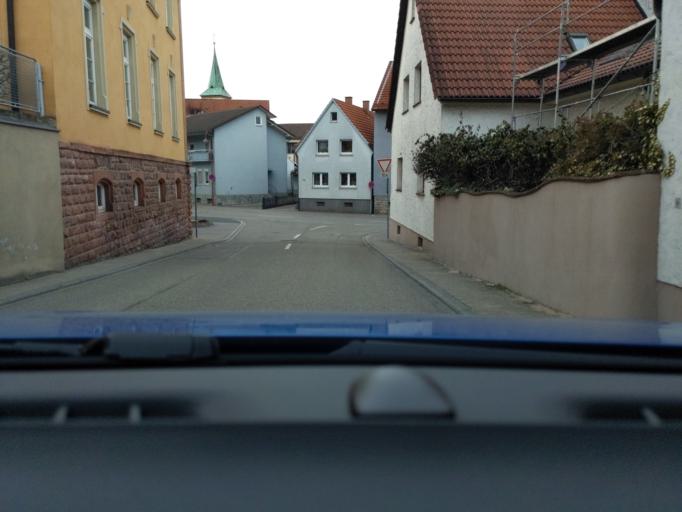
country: DE
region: Baden-Wuerttemberg
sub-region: Karlsruhe Region
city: Dielheim
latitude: 49.2819
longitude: 8.7369
